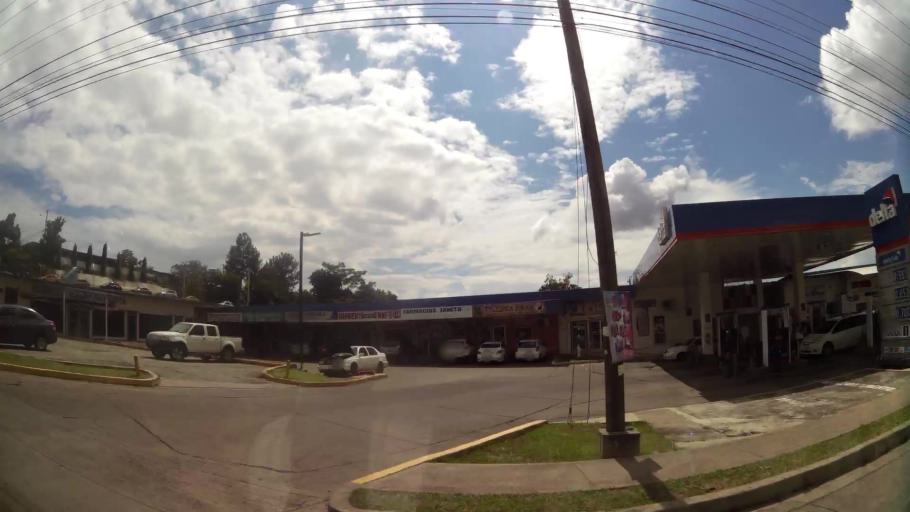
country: PA
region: Panama
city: Vista Alegre
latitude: 8.9262
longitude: -79.7089
